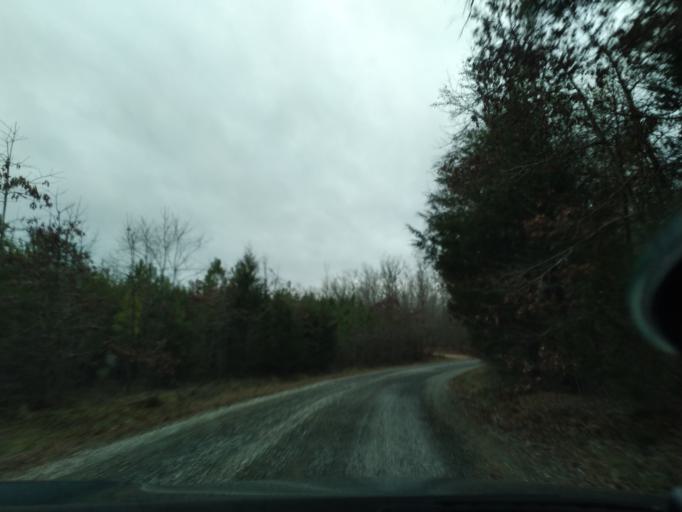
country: US
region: Virginia
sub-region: Buckingham County
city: Buckingham
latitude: 37.4296
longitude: -78.6560
